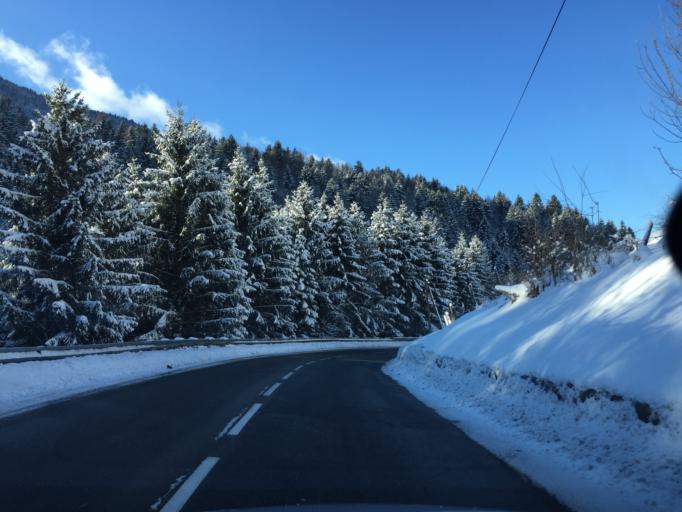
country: FR
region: Rhone-Alpes
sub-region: Departement de la Haute-Savoie
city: Saint-Paul-en-Chablais
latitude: 46.3353
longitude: 6.6375
